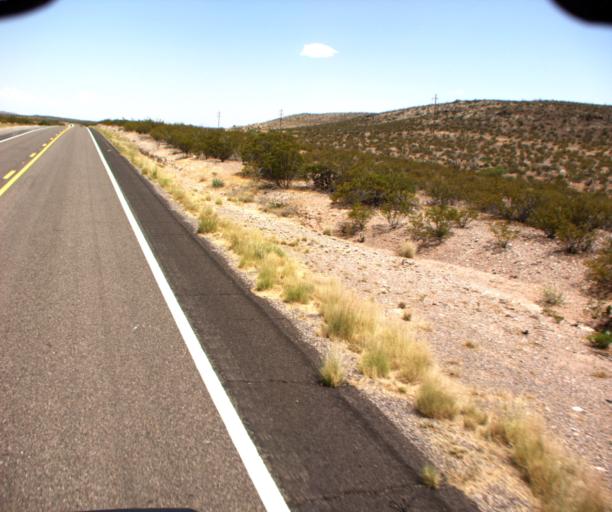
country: US
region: Arizona
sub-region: Graham County
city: Swift Trail Junction
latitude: 32.7519
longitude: -109.4072
